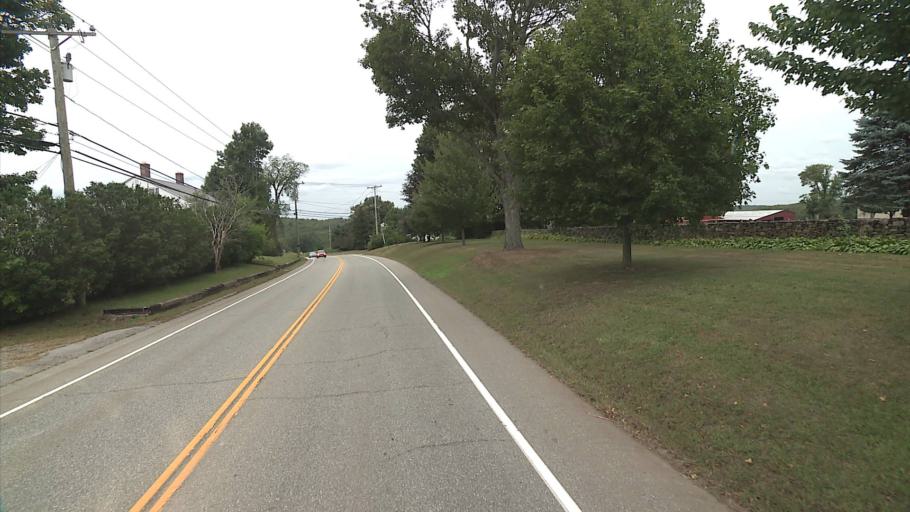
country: US
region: Connecticut
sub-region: Tolland County
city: Hebron
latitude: 41.6853
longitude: -72.4181
